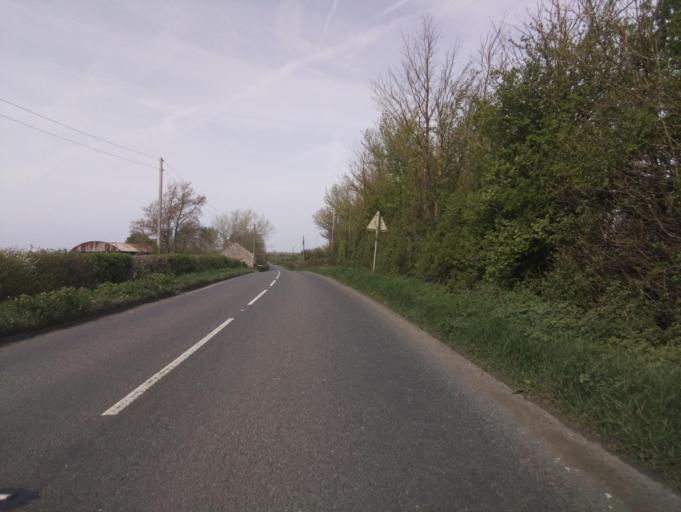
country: GB
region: England
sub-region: Somerset
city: Street
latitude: 51.1147
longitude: -2.7722
